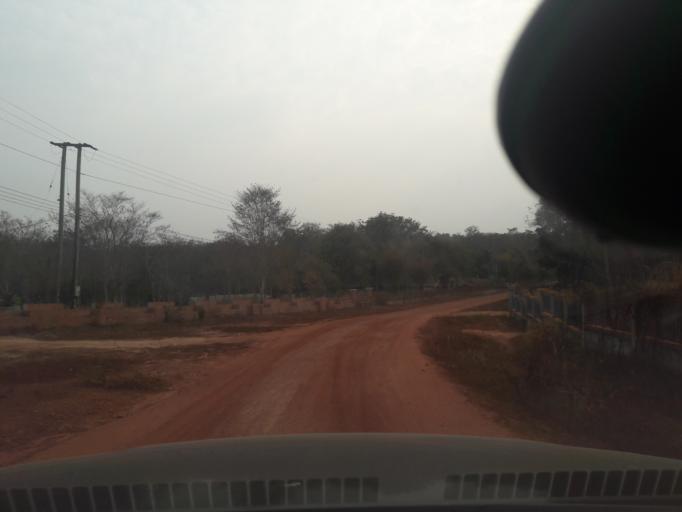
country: TH
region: Nong Khai
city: Si Chiang Mai
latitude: 18.0545
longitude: 102.4928
